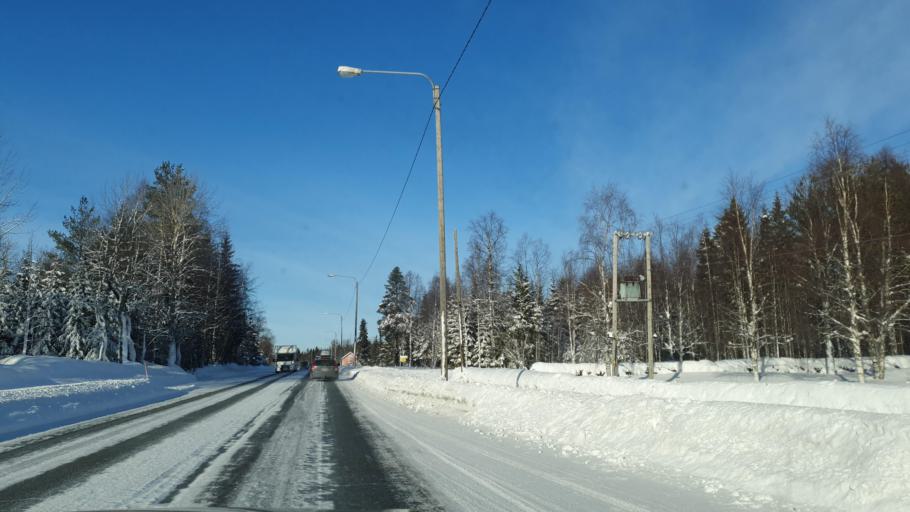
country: FI
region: Lapland
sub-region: Kemi-Tornio
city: Tornio
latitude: 65.9495
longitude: 24.0719
